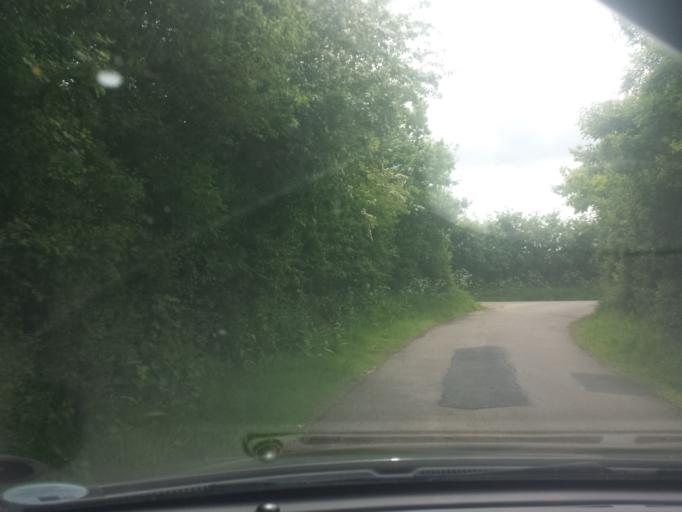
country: GB
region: England
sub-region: Essex
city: Little Clacton
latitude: 51.8710
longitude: 1.1428
